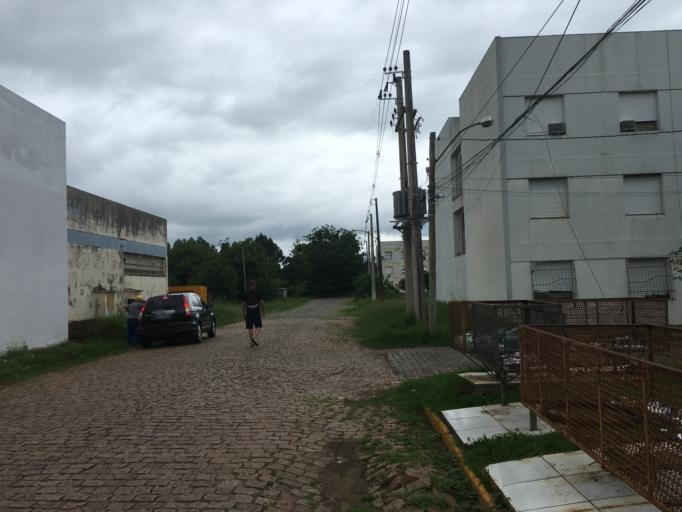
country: BR
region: Rio Grande do Sul
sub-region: Santa Maria
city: Santa Maria
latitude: -29.7175
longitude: -53.7141
